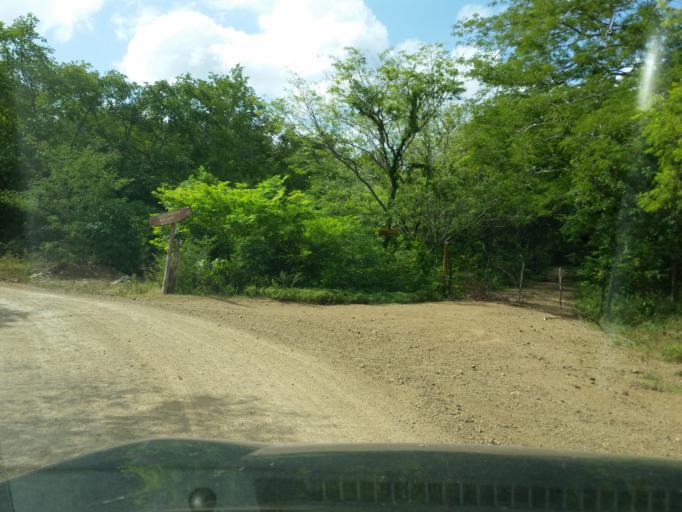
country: NI
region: Rivas
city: San Juan del Sur
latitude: 11.2108
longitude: -85.8391
